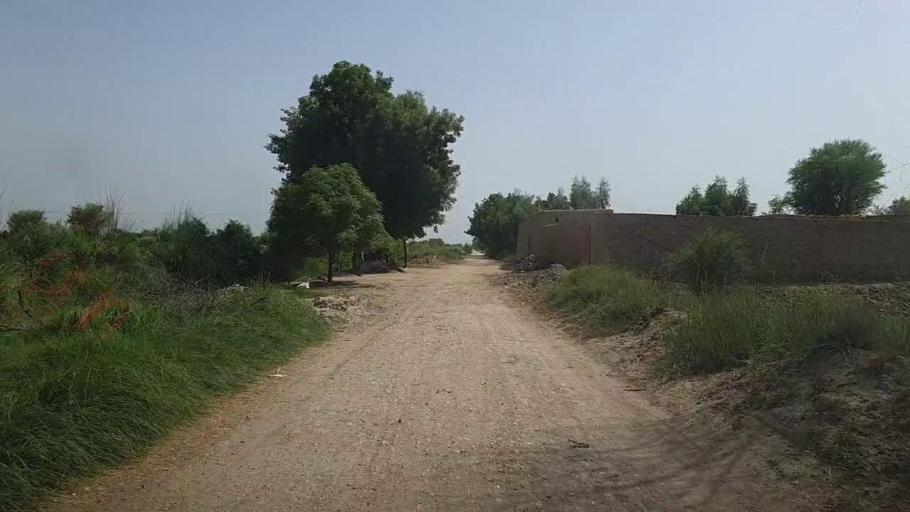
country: PK
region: Sindh
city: Pad Idan
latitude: 26.7942
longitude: 68.3291
